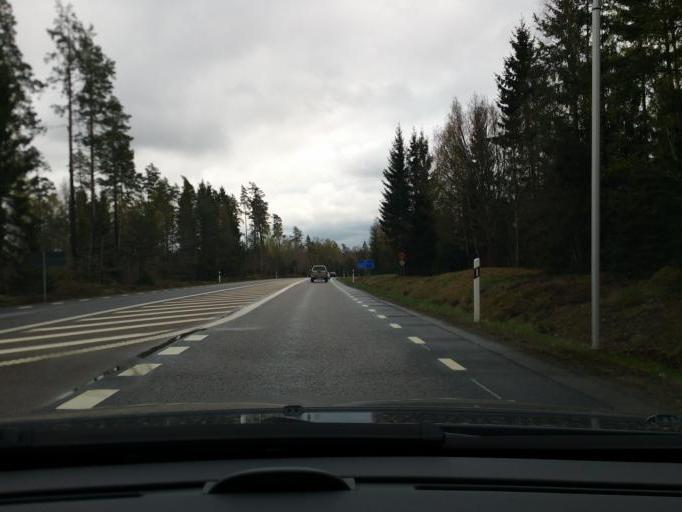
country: SE
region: Kronoberg
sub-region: Vaxjo Kommun
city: Ingelstad
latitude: 56.8085
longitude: 14.8860
